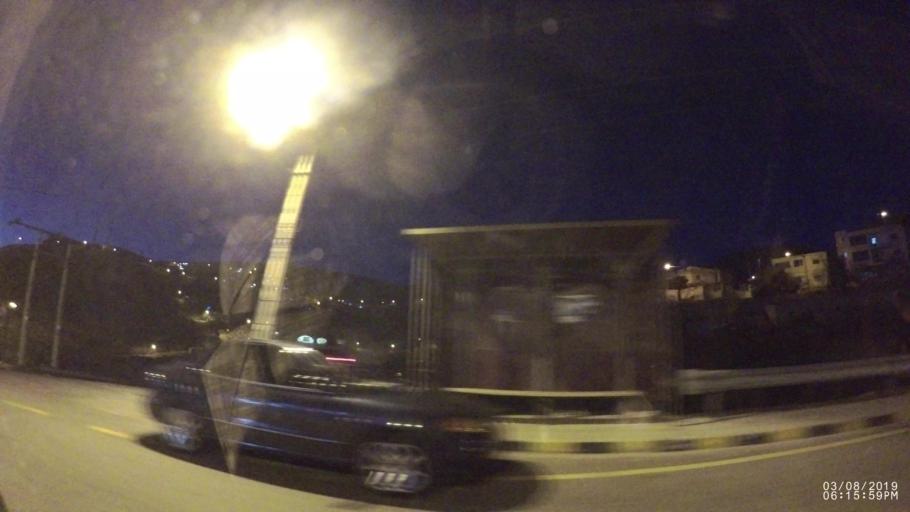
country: JO
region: Ma'an
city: Petra
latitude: 30.3262
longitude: 35.4946
